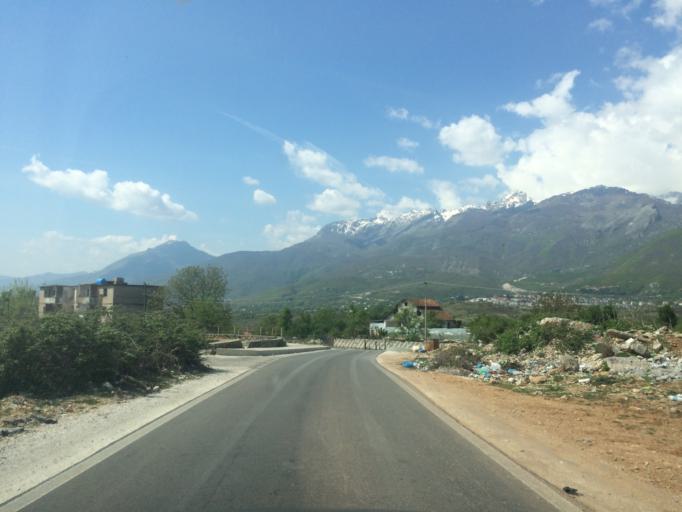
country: AL
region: Kukes
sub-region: Rrethi i Tropojes
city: Llugaj
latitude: 42.3604
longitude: 20.1059
